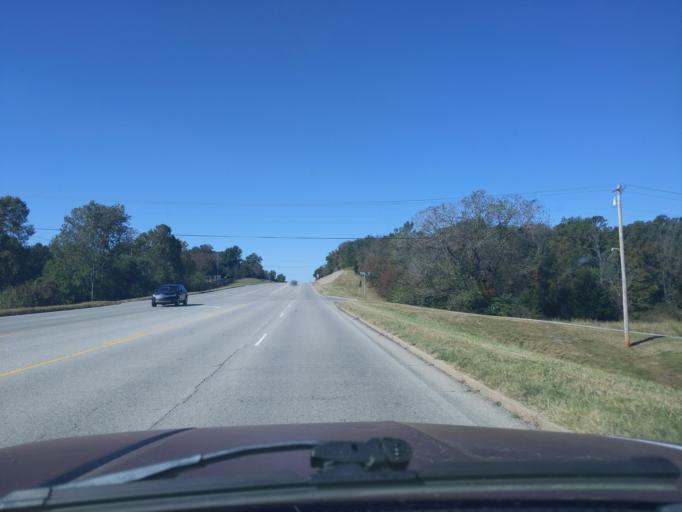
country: US
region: Oklahoma
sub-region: Creek County
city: Kiefer
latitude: 35.9885
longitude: -96.0647
